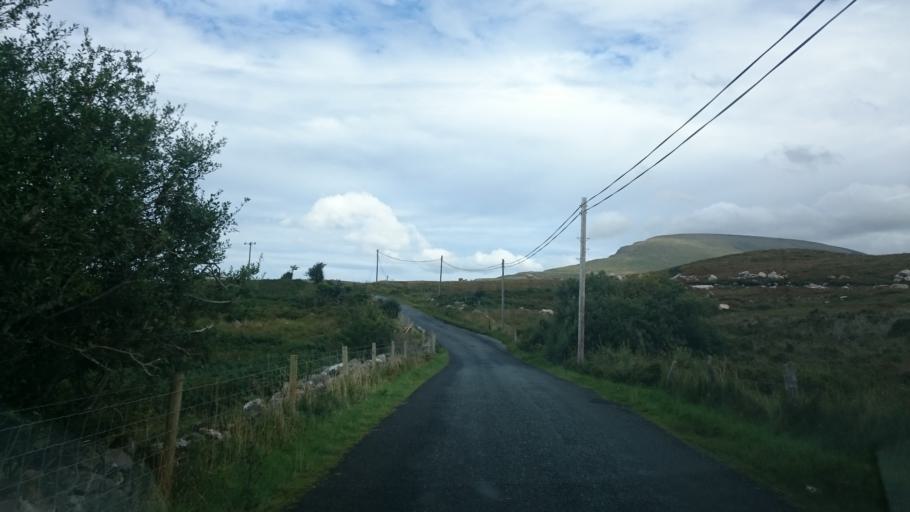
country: IE
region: Connaught
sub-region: Maigh Eo
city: Westport
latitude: 53.9155
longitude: -9.5536
